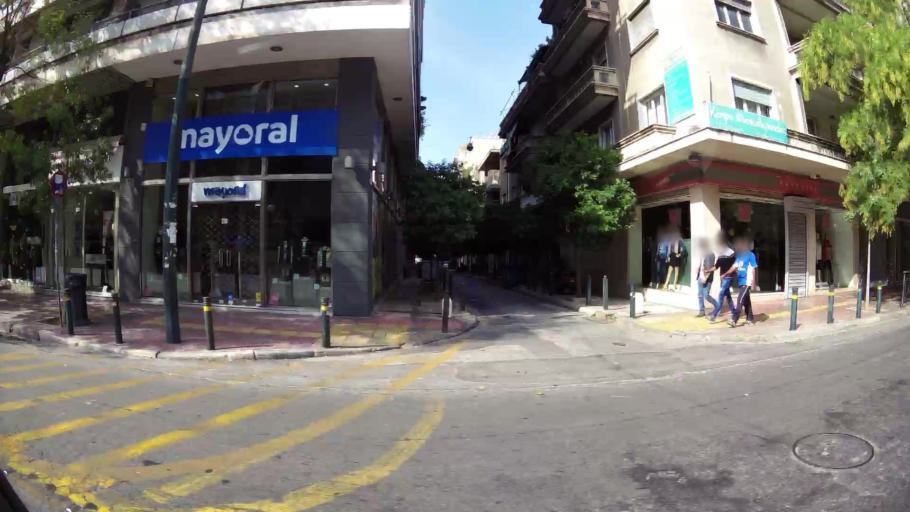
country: GR
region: Attica
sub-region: Nomarchia Athinas
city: Kipseli
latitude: 37.9987
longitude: 23.7330
